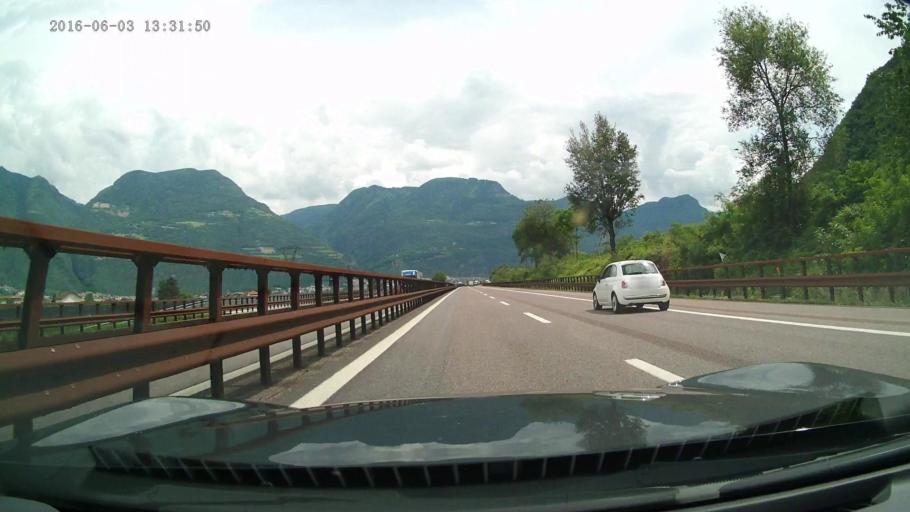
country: IT
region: Trentino-Alto Adige
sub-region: Bolzano
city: San Giacomo
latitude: 46.4454
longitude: 11.3129
